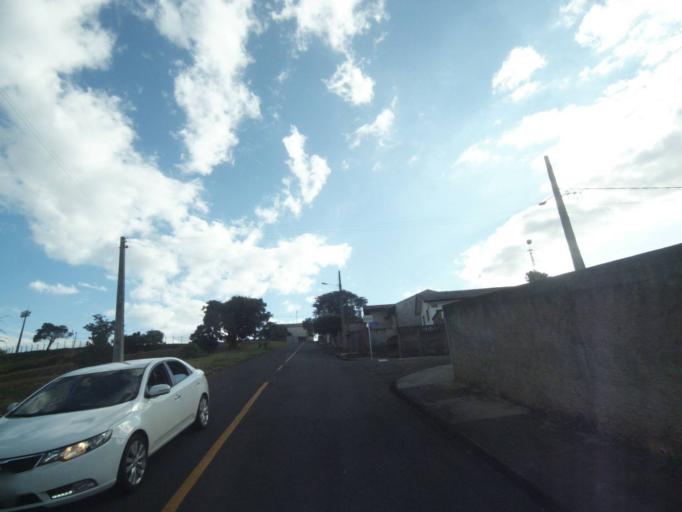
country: BR
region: Parana
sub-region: Telemaco Borba
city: Telemaco Borba
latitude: -24.3406
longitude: -50.6182
